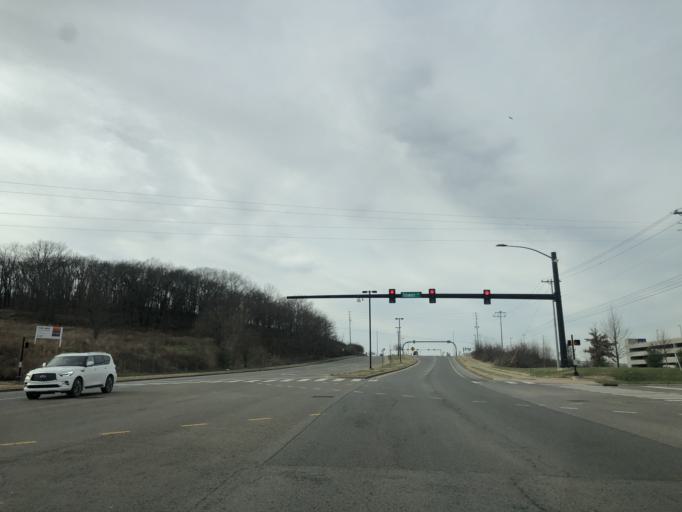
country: US
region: Tennessee
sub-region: Williamson County
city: Franklin
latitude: 35.9333
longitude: -86.8144
